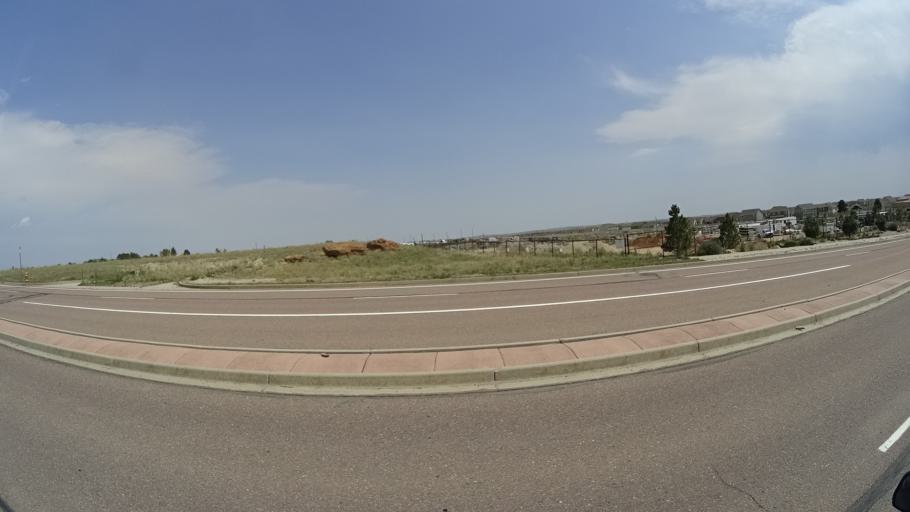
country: US
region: Colorado
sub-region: El Paso County
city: Cimarron Hills
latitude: 38.9355
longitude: -104.7123
